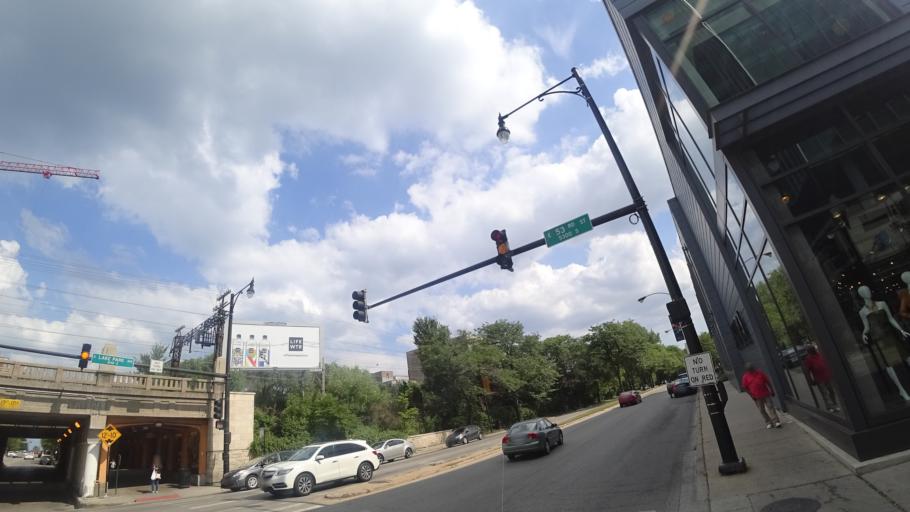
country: US
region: Illinois
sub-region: Cook County
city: Chicago
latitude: 41.7996
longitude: -87.5876
